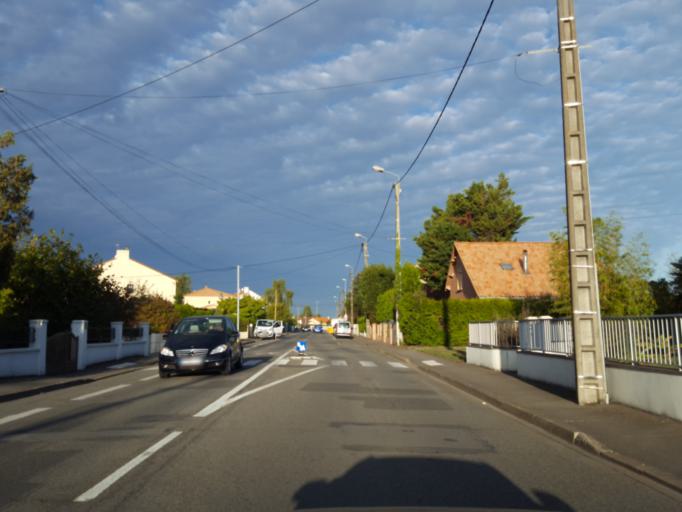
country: FR
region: Pays de la Loire
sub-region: Departement de la Loire-Atlantique
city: Saint-Sebastien-sur-Loire
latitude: 47.1974
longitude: -1.4953
